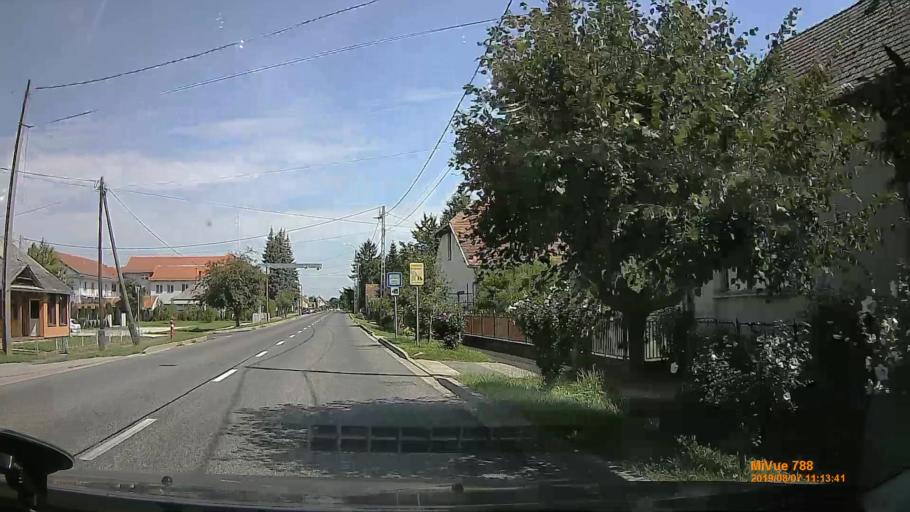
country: HU
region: Zala
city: Lenti
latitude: 46.7014
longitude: 16.5490
